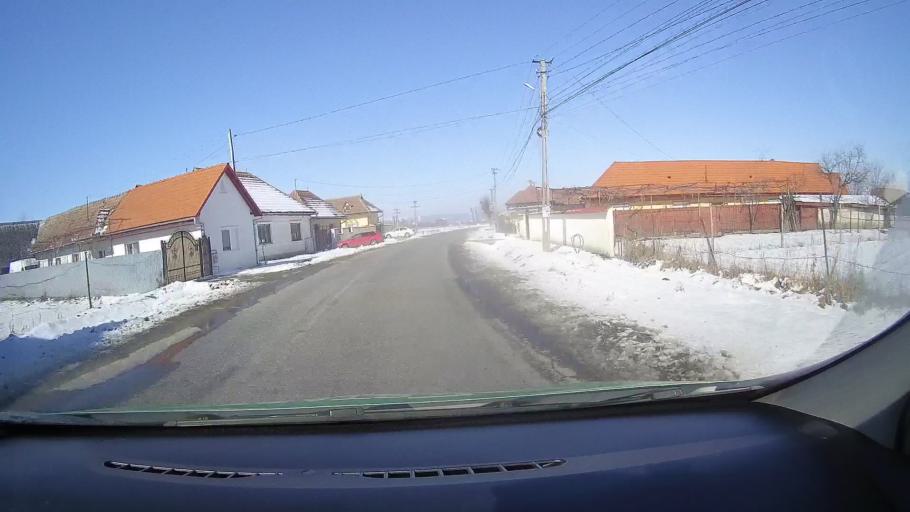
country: RO
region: Brasov
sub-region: Comuna Harseni
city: Harseni
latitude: 45.7930
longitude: 24.9960
